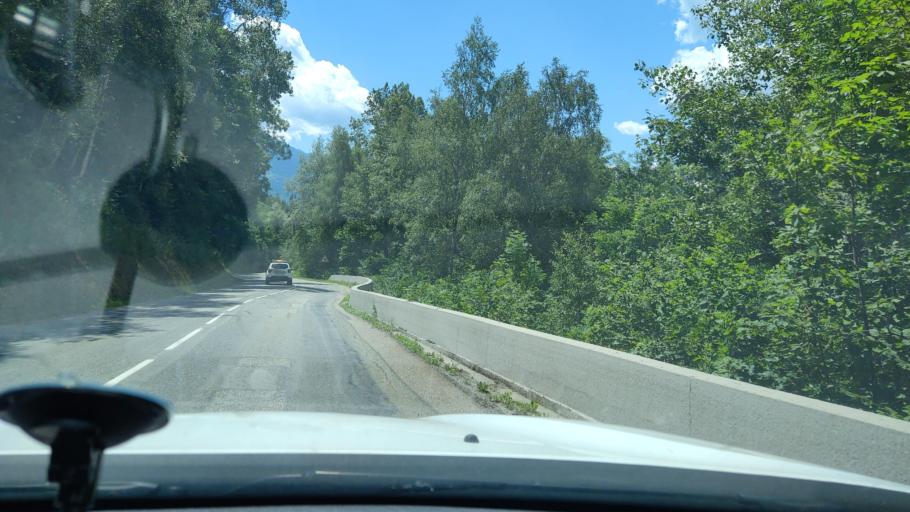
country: FR
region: Rhone-Alpes
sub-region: Departement de la Savoie
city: Bourg-Saint-Maurice
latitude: 45.6033
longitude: 6.7755
